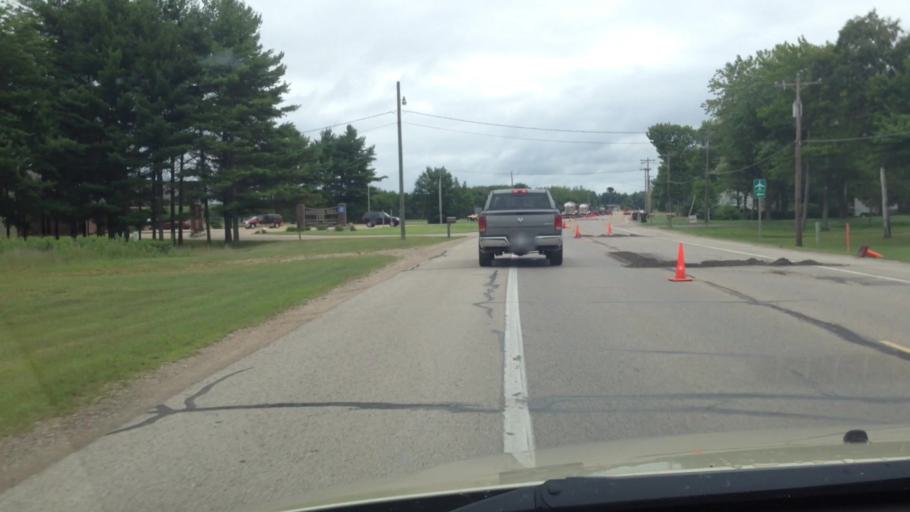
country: US
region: Michigan
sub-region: Delta County
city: Escanaba
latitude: 45.7128
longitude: -87.0904
